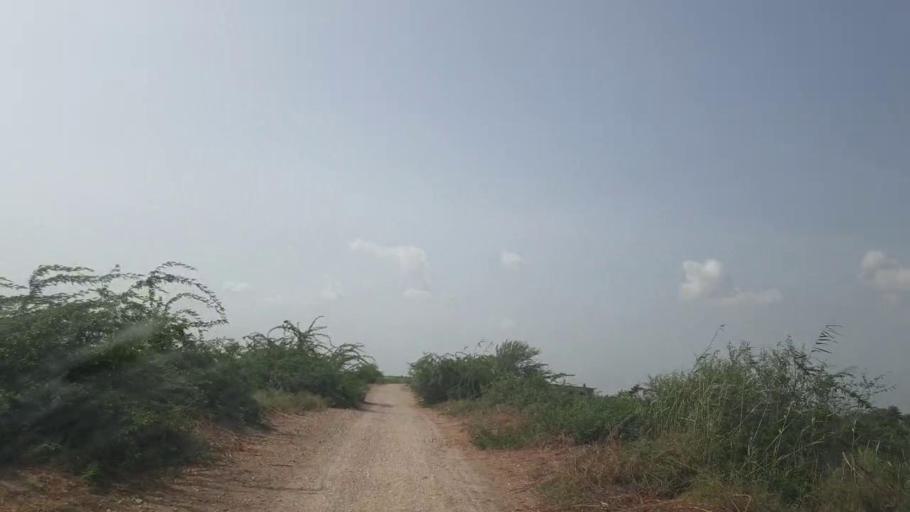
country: PK
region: Sindh
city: Tando Bago
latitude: 24.7689
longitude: 69.1312
